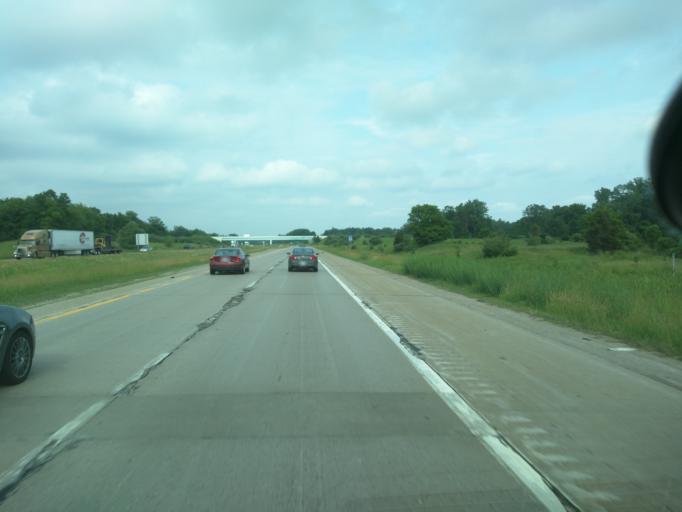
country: US
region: Michigan
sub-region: Clinton County
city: Bath
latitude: 42.8023
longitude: -84.4894
